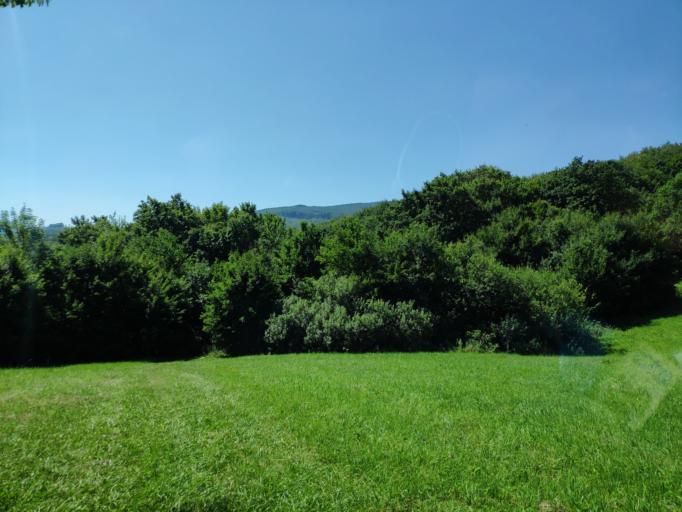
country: SK
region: Kosicky
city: Secovce
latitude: 48.6365
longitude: 21.4582
